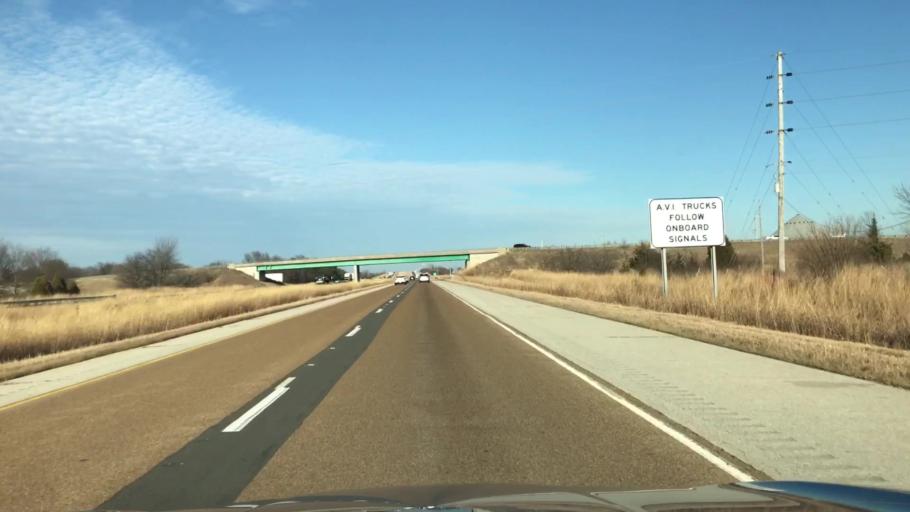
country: US
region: Illinois
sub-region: Montgomery County
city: Litchfield
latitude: 39.2032
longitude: -89.6606
